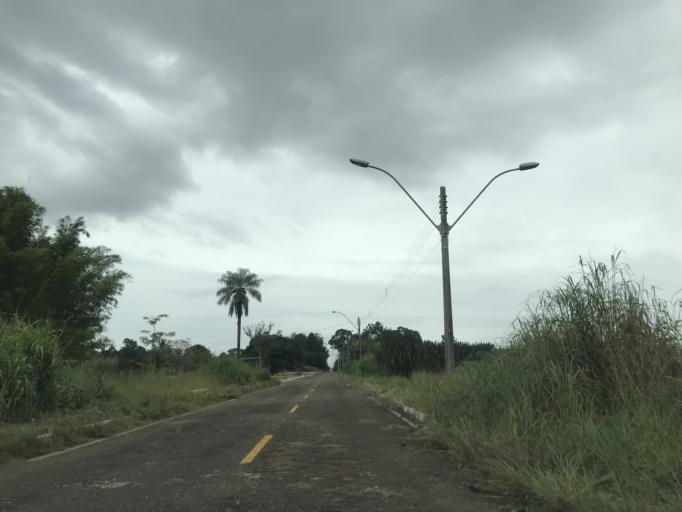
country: BR
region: Federal District
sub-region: Brasilia
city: Brasilia
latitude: -15.8905
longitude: -47.9306
